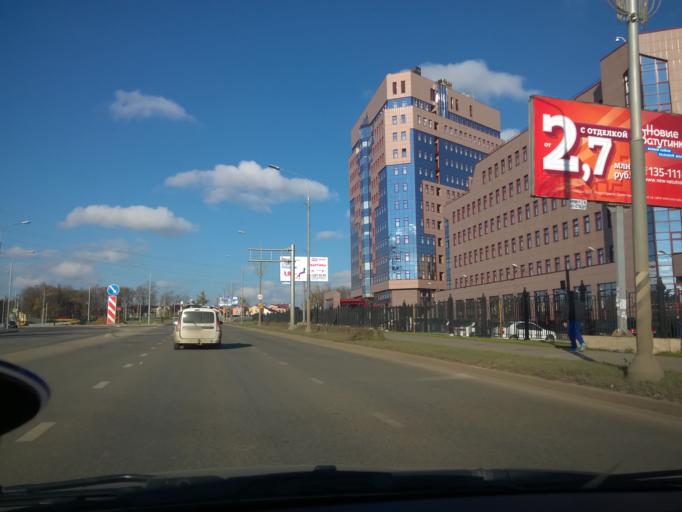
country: RU
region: Moskovskaya
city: Kommunarka
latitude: 55.5798
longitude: 37.4690
